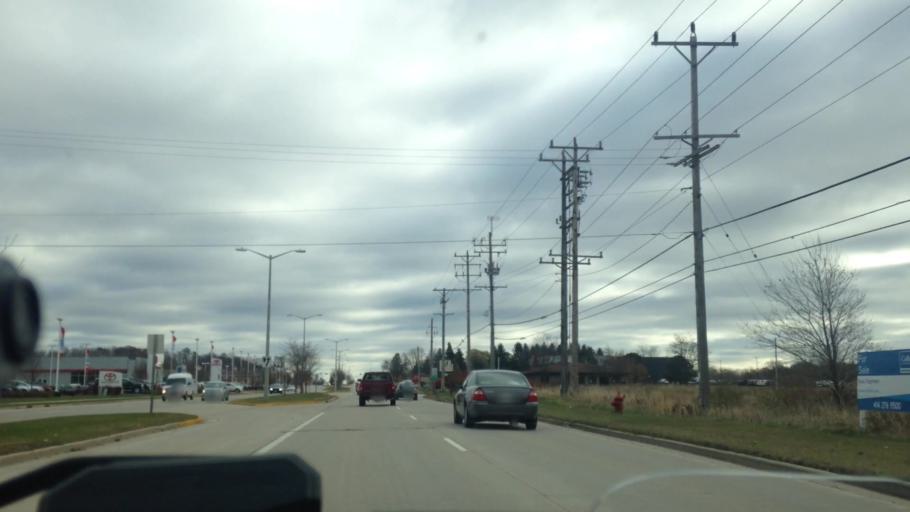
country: US
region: Wisconsin
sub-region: Washington County
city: West Bend
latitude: 43.4271
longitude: -88.2228
